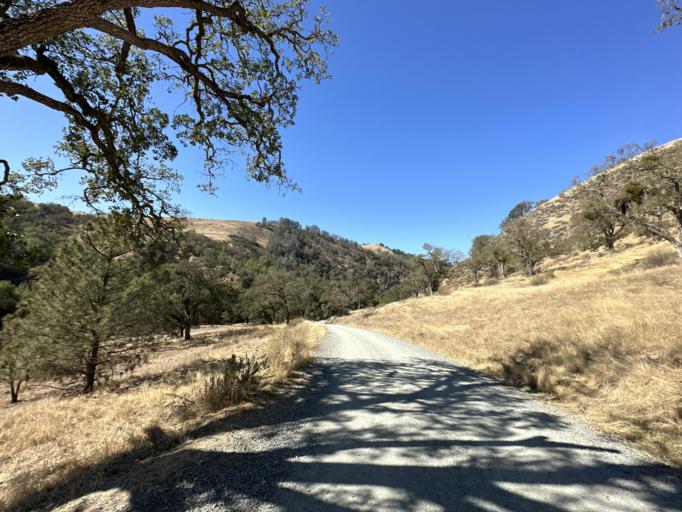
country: US
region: California
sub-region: Santa Clara County
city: Milpitas
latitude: 37.5041
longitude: -121.8225
